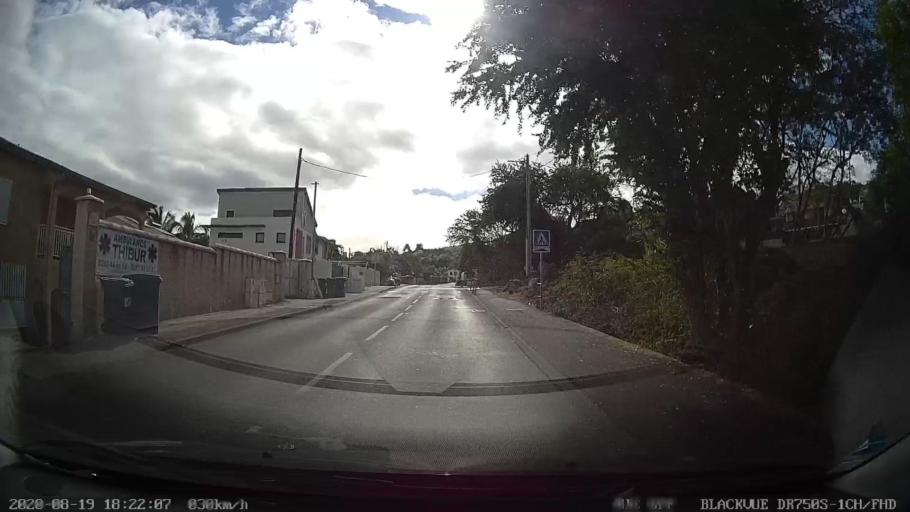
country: RE
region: Reunion
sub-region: Reunion
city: La Possession
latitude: -20.9554
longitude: 55.3374
